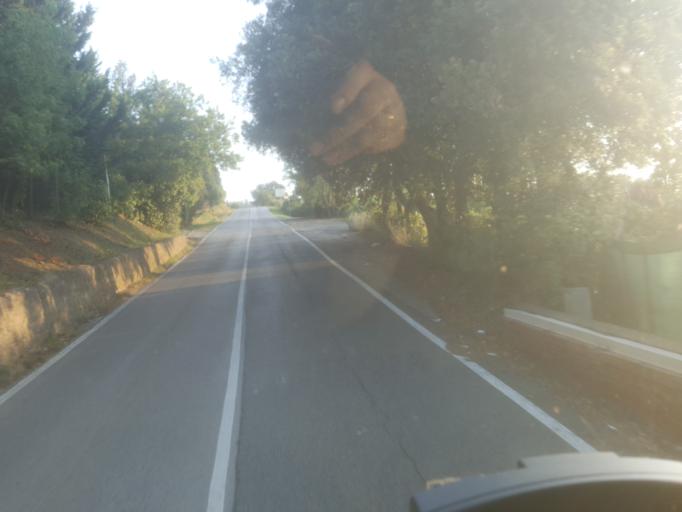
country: IT
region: Tuscany
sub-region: Province of Florence
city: Montaione
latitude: 43.5405
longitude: 10.9272
